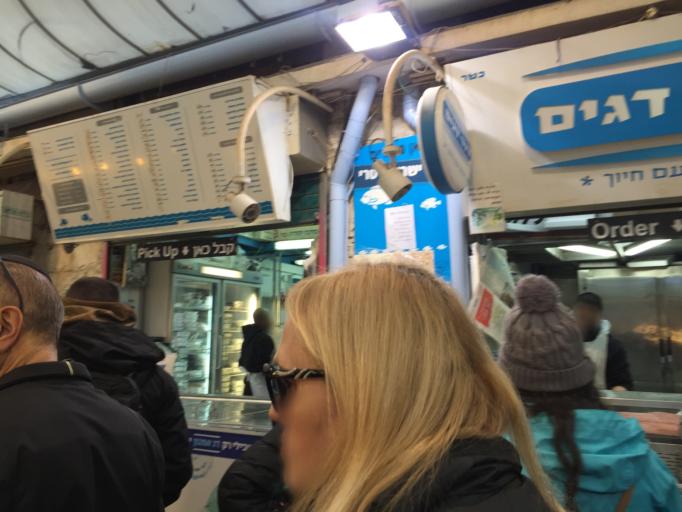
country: IL
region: Jerusalem
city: West Jerusalem
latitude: 31.7844
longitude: 35.2128
